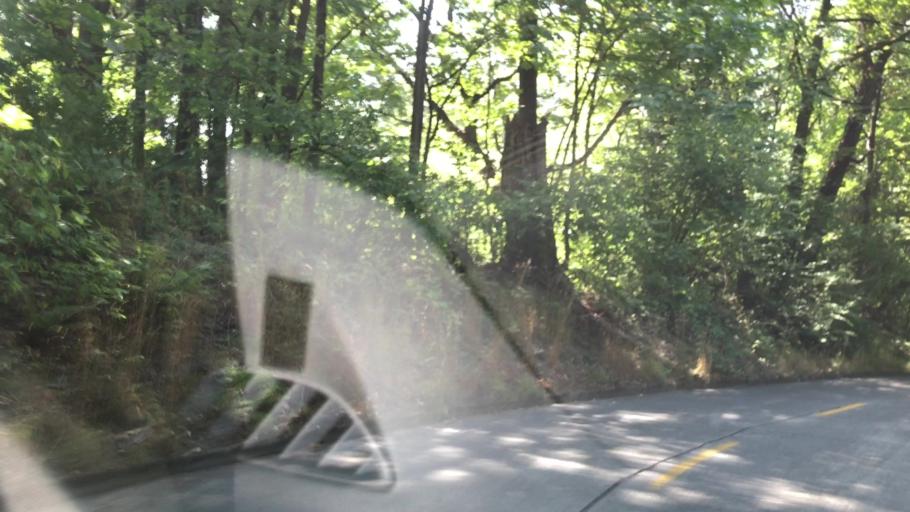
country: US
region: Washington
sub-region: King County
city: Seattle
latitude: 47.6004
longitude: -122.2895
